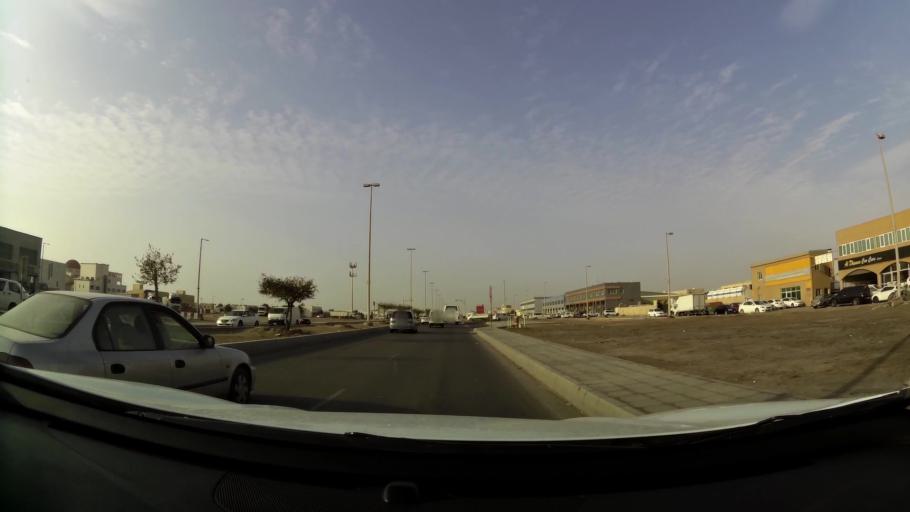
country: AE
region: Abu Dhabi
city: Abu Dhabi
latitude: 24.3482
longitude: 54.5172
